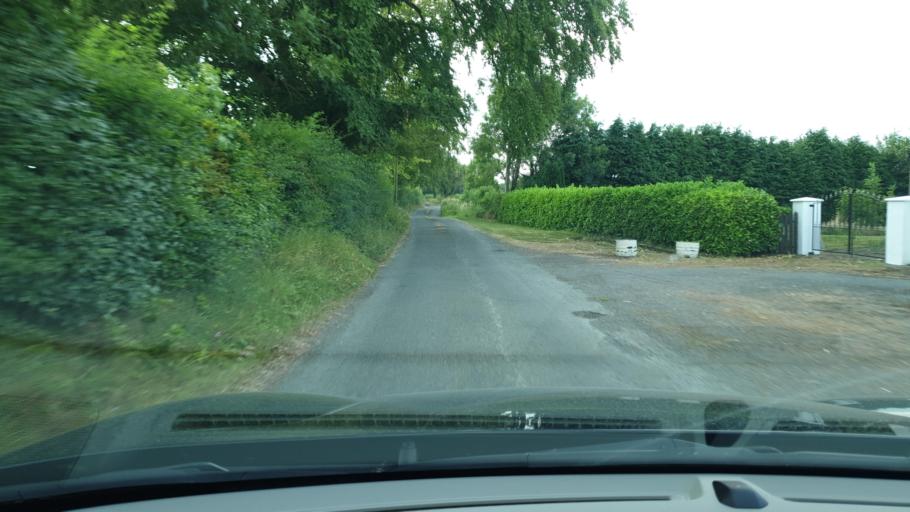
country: IE
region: Leinster
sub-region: An Mhi
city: Ratoath
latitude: 53.4710
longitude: -6.4387
